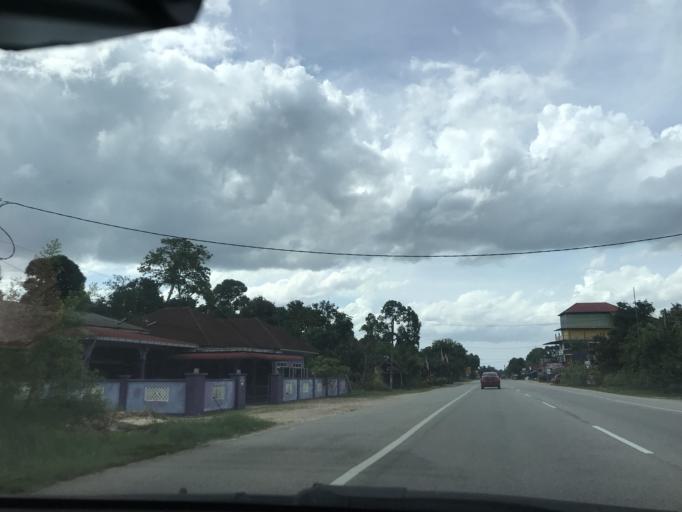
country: MY
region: Kelantan
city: Kampong Pangkal Kalong
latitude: 5.9232
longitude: 102.1896
